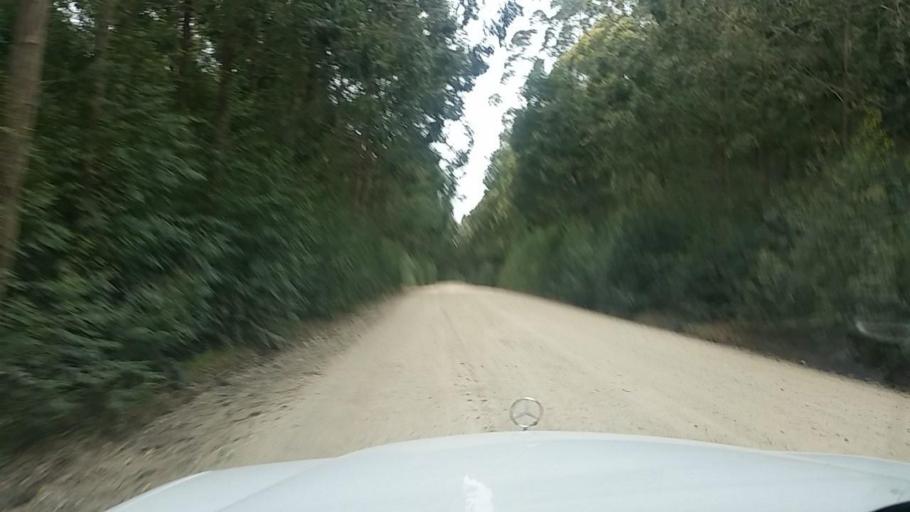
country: ZA
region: Western Cape
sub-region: Eden District Municipality
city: Knysna
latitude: -33.9812
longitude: 23.1392
